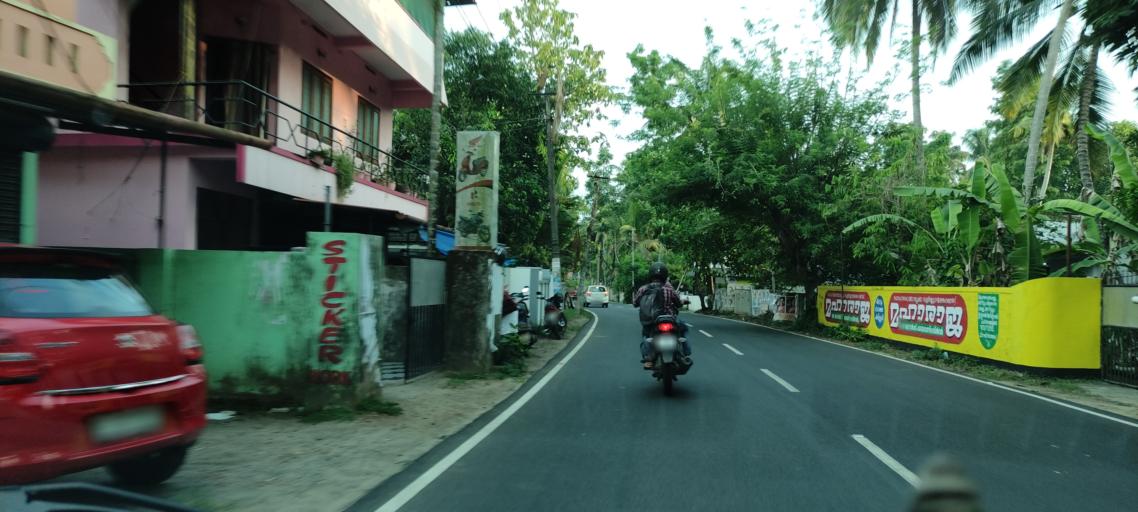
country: IN
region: Kerala
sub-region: Alappuzha
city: Arukutti
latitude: 9.8664
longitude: 76.3238
